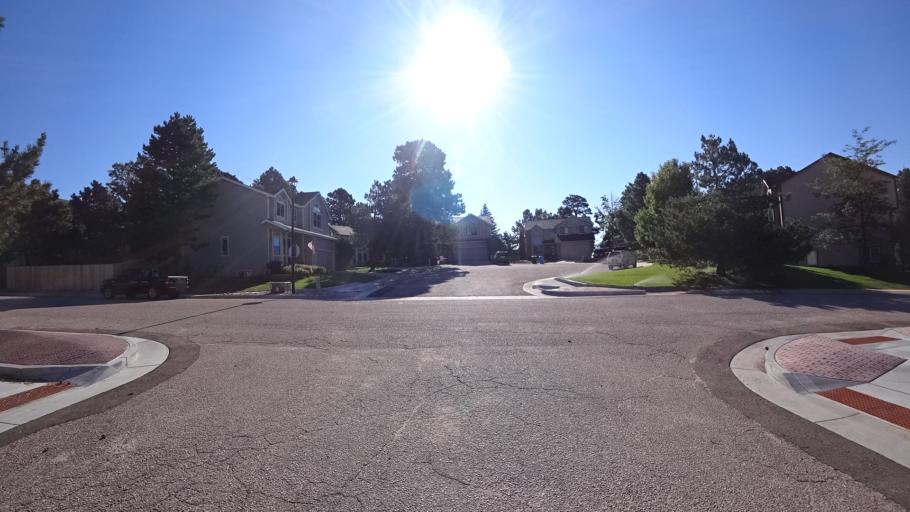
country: US
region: Colorado
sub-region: El Paso County
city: Air Force Academy
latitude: 38.9719
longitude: -104.7911
